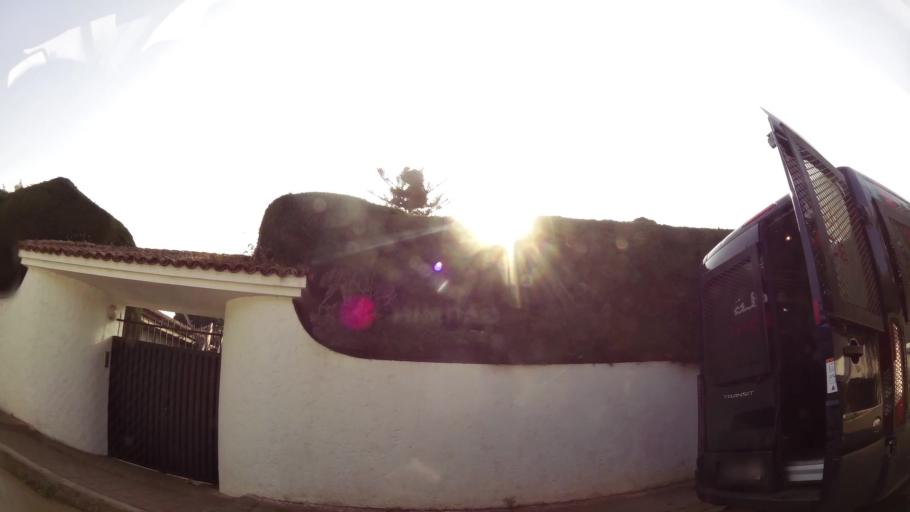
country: MA
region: Rabat-Sale-Zemmour-Zaer
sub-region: Rabat
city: Rabat
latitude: 33.9404
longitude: -6.8194
